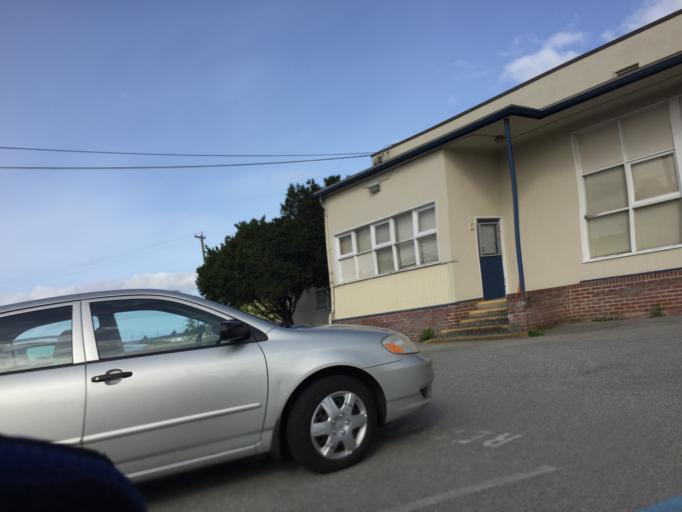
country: CA
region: British Columbia
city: Richmond
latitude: 49.1910
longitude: -123.1496
